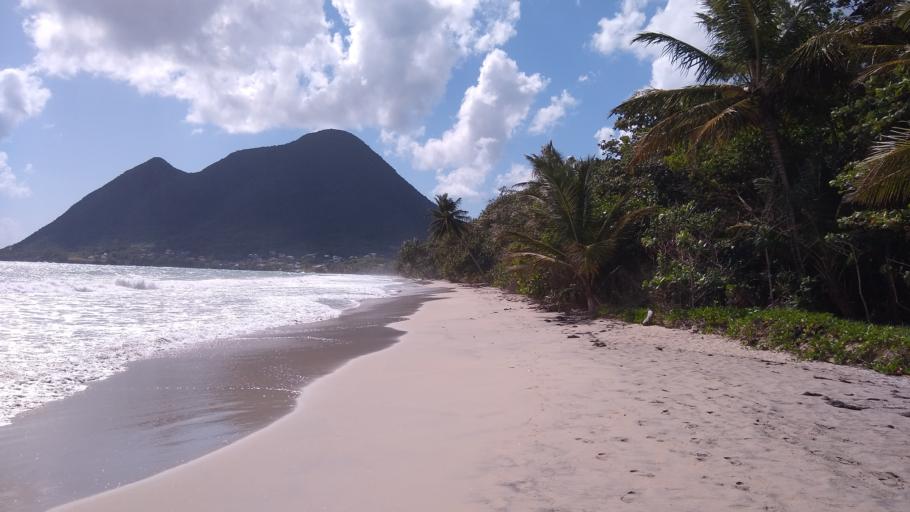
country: MQ
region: Martinique
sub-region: Martinique
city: Les Trois-Ilets
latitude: 14.4760
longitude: -61.0357
